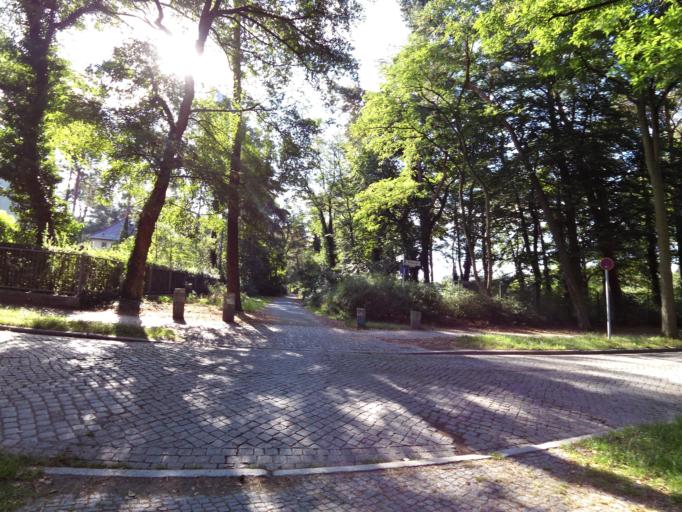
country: DE
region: Berlin
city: Zehlendorf Bezirk
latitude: 52.4476
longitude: 13.2492
